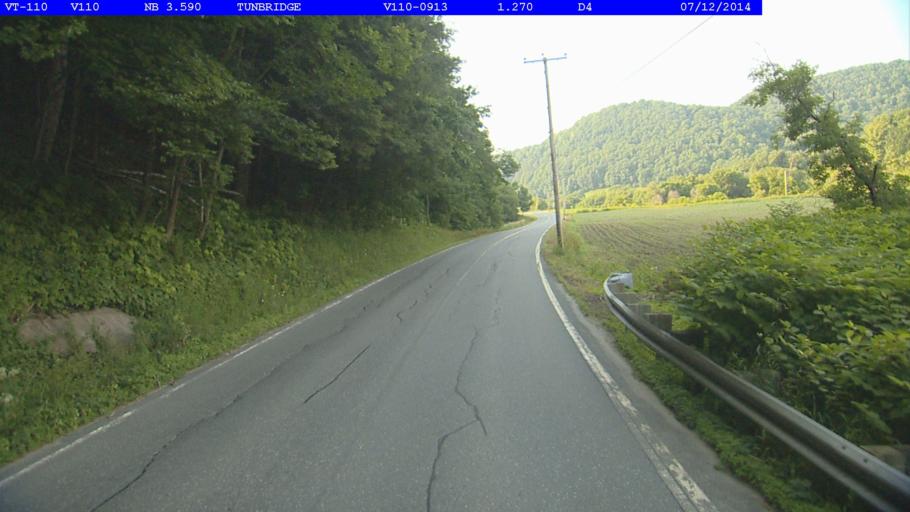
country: US
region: Vermont
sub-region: Orange County
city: Chelsea
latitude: 43.8691
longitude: -72.4993
